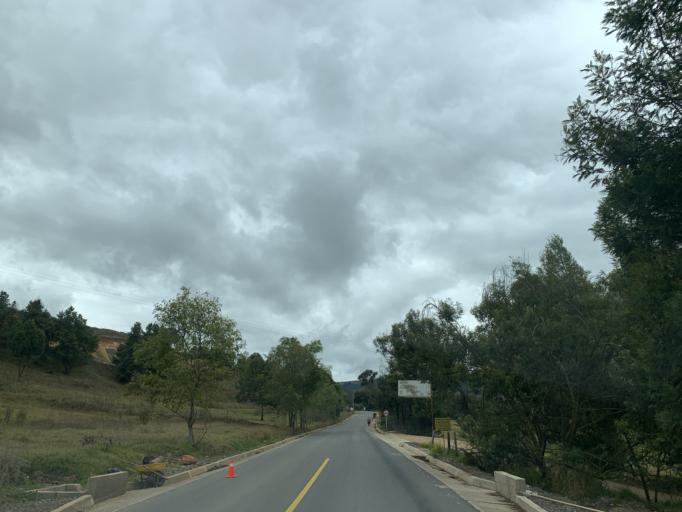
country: CO
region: Boyaca
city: Tunja
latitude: 5.5282
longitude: -73.3191
